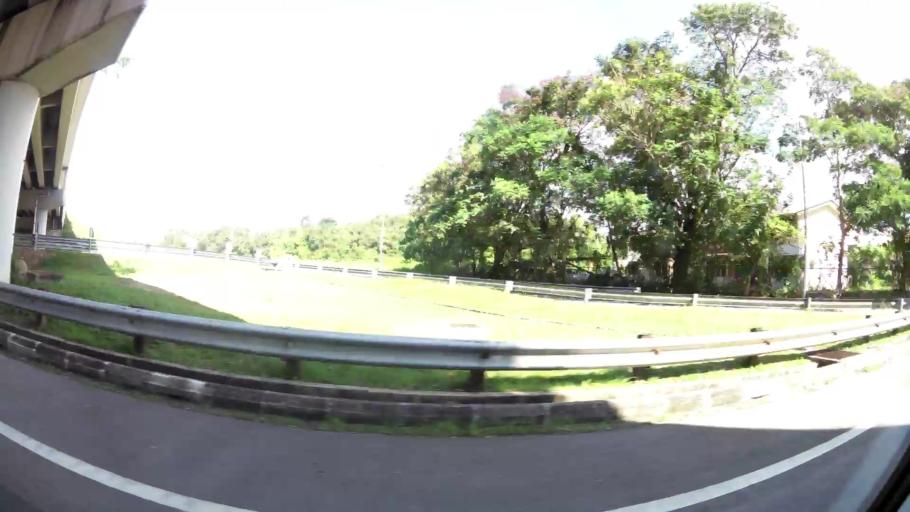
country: BN
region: Brunei and Muara
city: Bandar Seri Begawan
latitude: 4.9506
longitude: 114.9442
